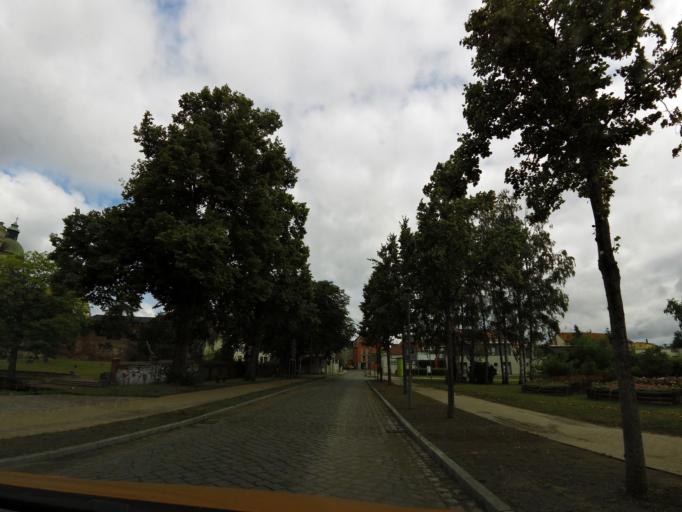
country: DE
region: Mecklenburg-Vorpommern
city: Guestrow
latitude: 53.7905
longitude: 12.1796
